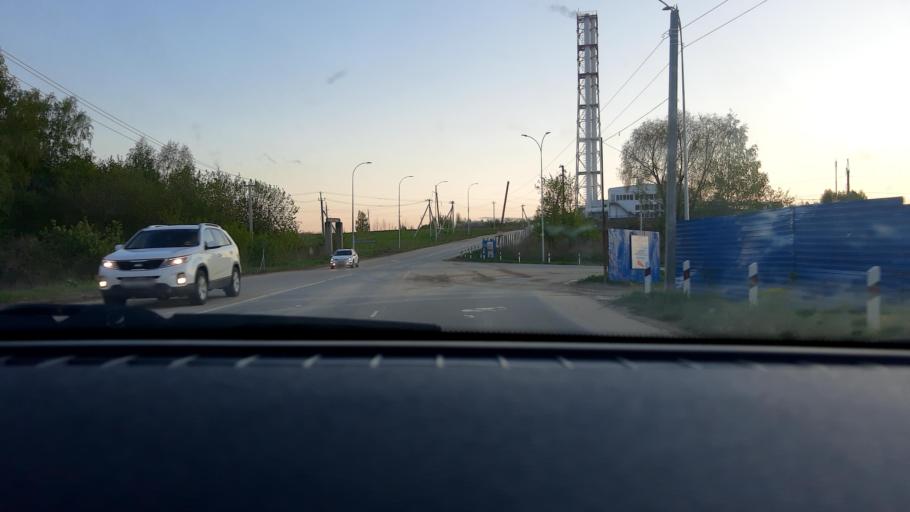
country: RU
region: Nizjnij Novgorod
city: Afonino
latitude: 56.2430
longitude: 44.0615
